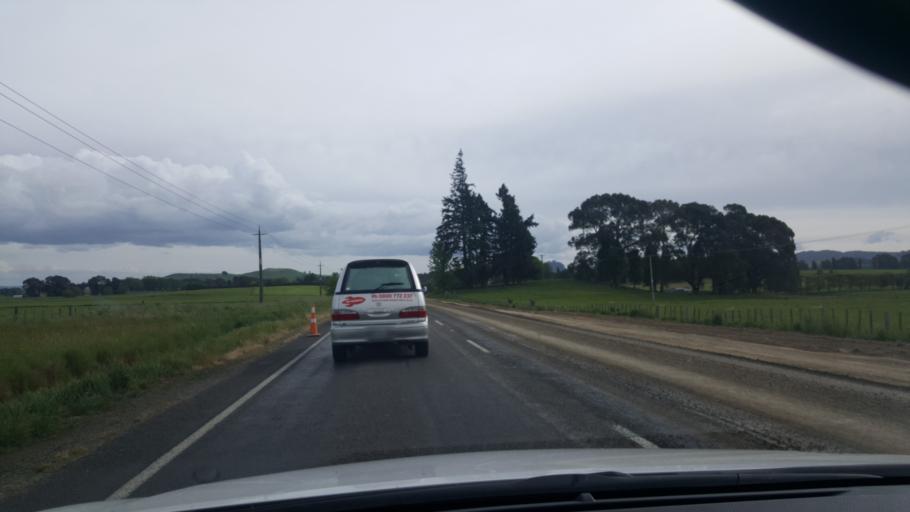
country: NZ
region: Bay of Plenty
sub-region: Rotorua District
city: Rotorua
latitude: -38.4064
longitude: 176.3261
